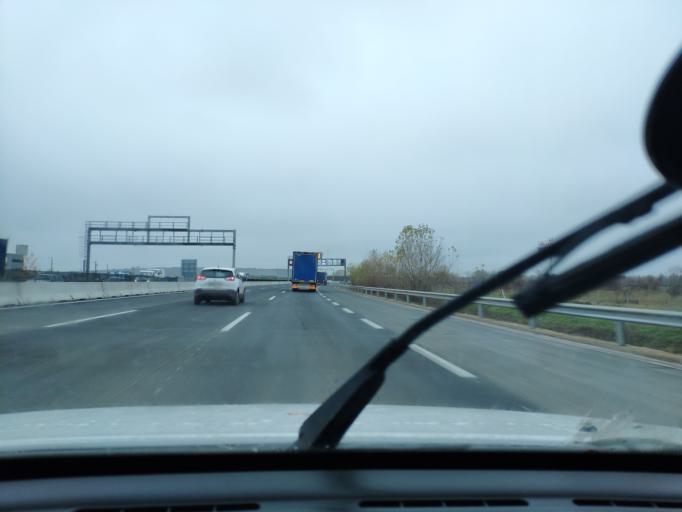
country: HU
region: Pest
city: Szigetszentmiklos
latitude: 47.3798
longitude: 19.0252
